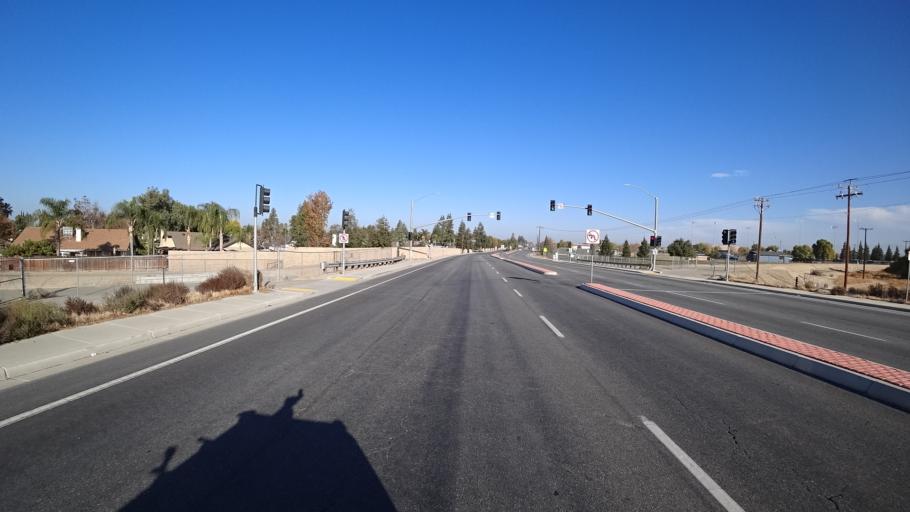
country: US
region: California
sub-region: Kern County
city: Rosedale
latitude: 35.3481
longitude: -119.1454
